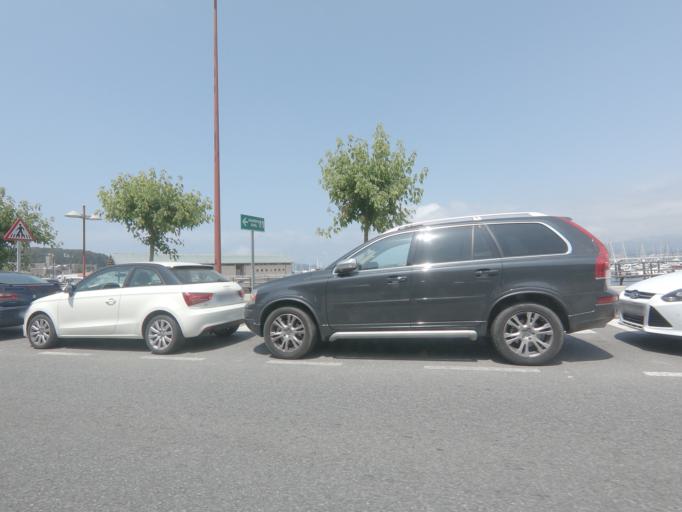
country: ES
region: Galicia
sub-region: Provincia de Pontevedra
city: Baiona
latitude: 42.1183
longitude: -8.8466
